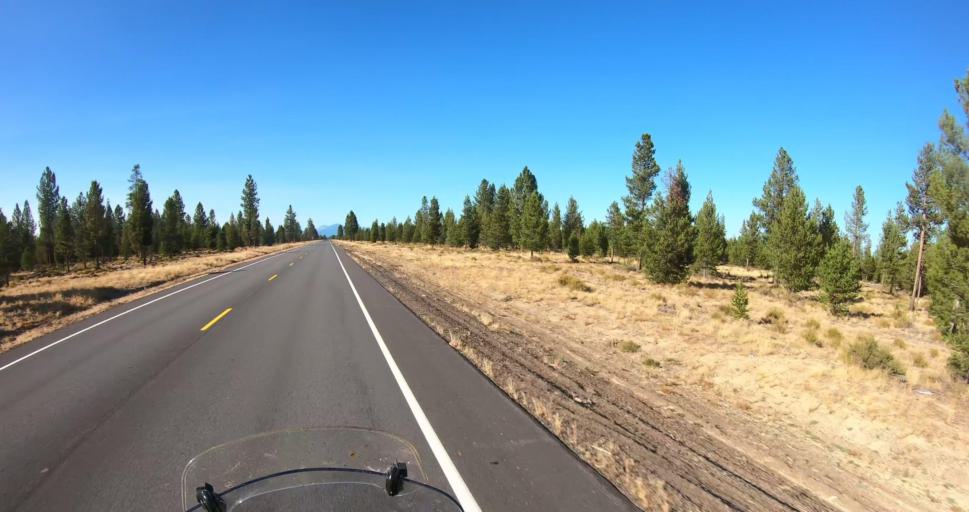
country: US
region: Oregon
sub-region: Deschutes County
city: La Pine
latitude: 43.6137
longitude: -121.5047
